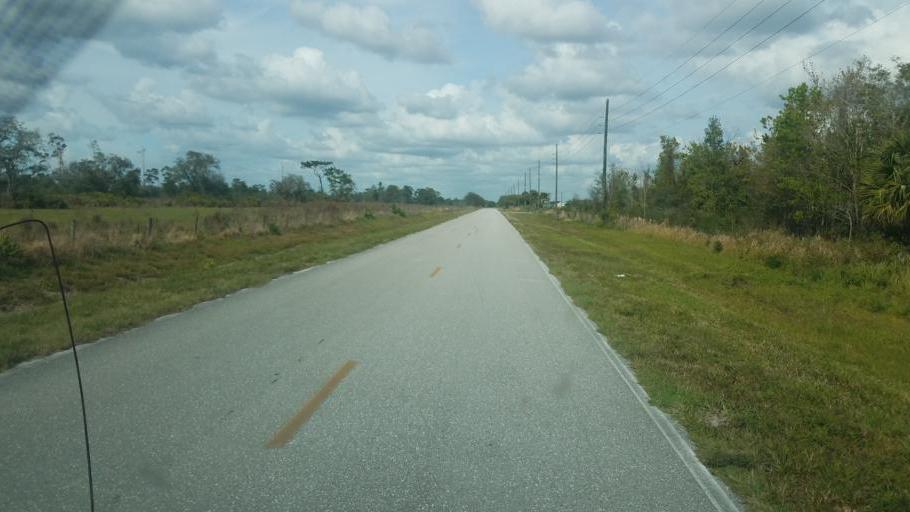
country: US
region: Florida
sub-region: Okeechobee County
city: Cypress Quarters
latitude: 27.5088
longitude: -80.7761
